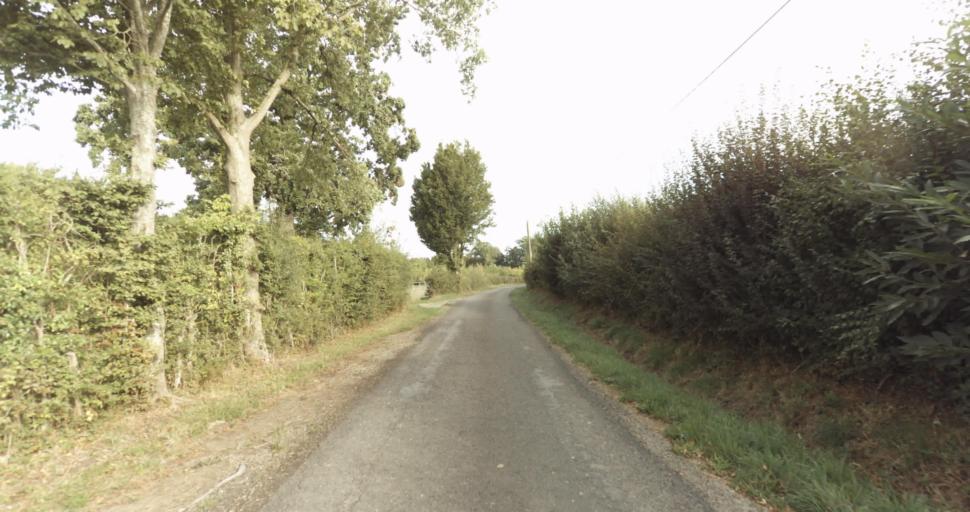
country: FR
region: Lower Normandy
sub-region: Departement de l'Orne
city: Gace
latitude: 48.8314
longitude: 0.2106
